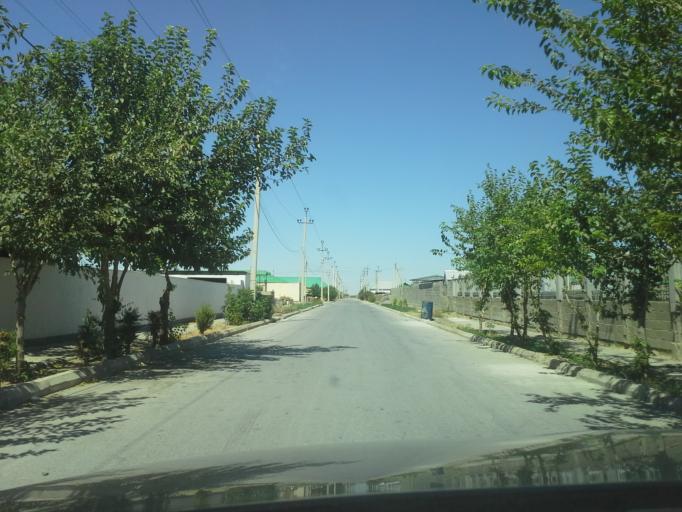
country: TM
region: Ahal
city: Abadan
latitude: 38.0596
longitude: 58.2052
